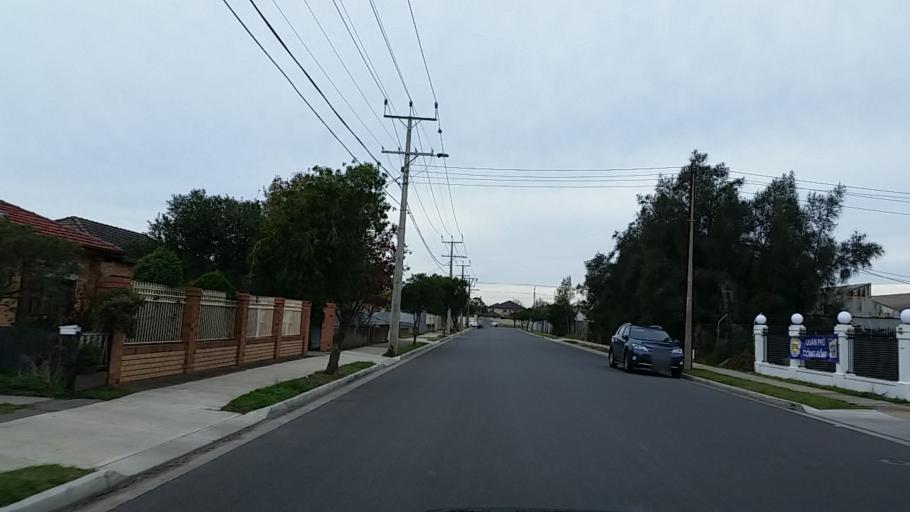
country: AU
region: South Australia
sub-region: Charles Sturt
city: Woodville North
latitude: -34.8525
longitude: 138.5448
